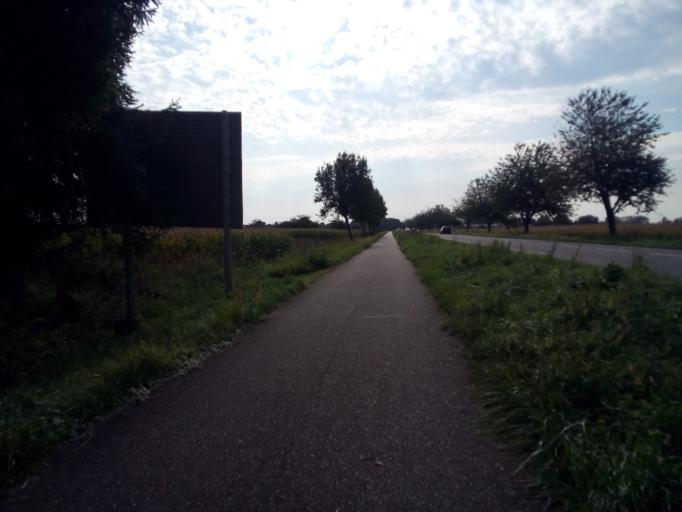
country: FR
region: Alsace
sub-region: Departement du Bas-Rhin
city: Herrlisheim
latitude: 48.7418
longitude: 7.9202
